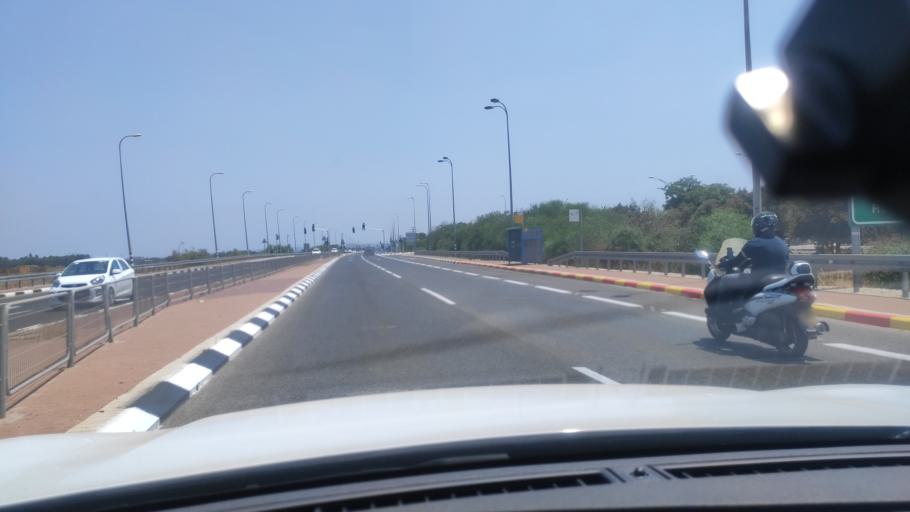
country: IL
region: Central District
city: Hod HaSharon
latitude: 32.1341
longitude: 34.9099
